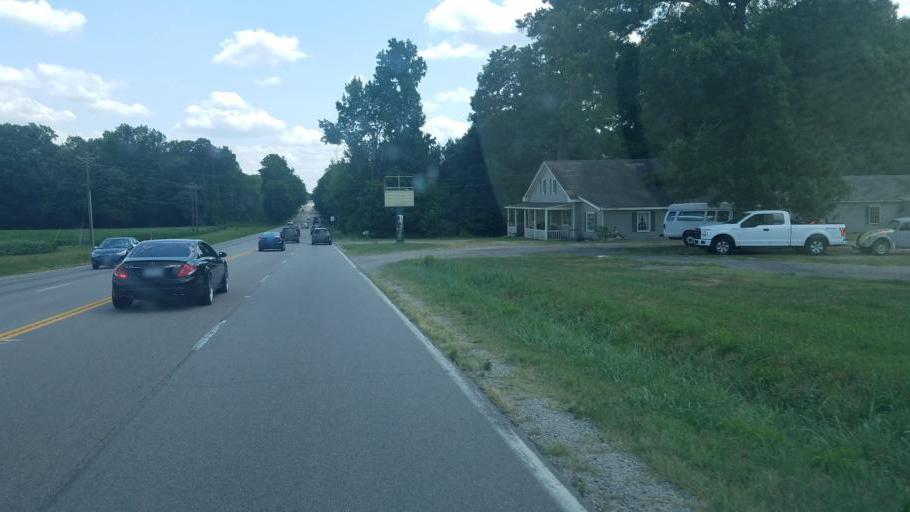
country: US
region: Virginia
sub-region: Prince George County
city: Prince George
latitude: 37.1690
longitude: -77.2956
